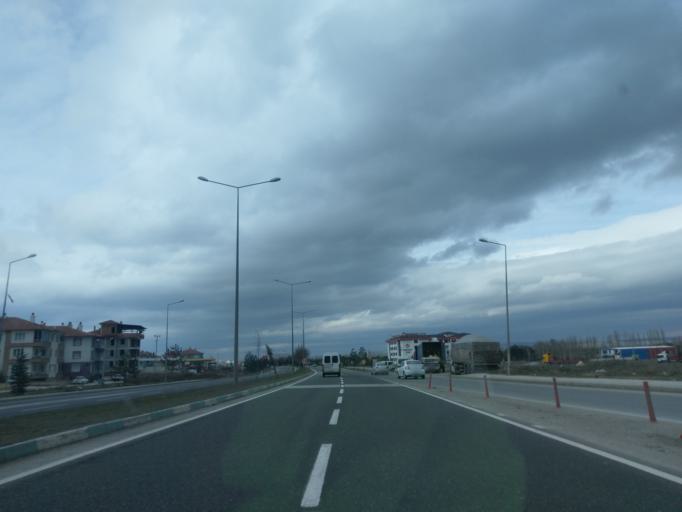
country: TR
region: Kuetahya
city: Kutahya
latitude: 39.4074
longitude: 30.0260
